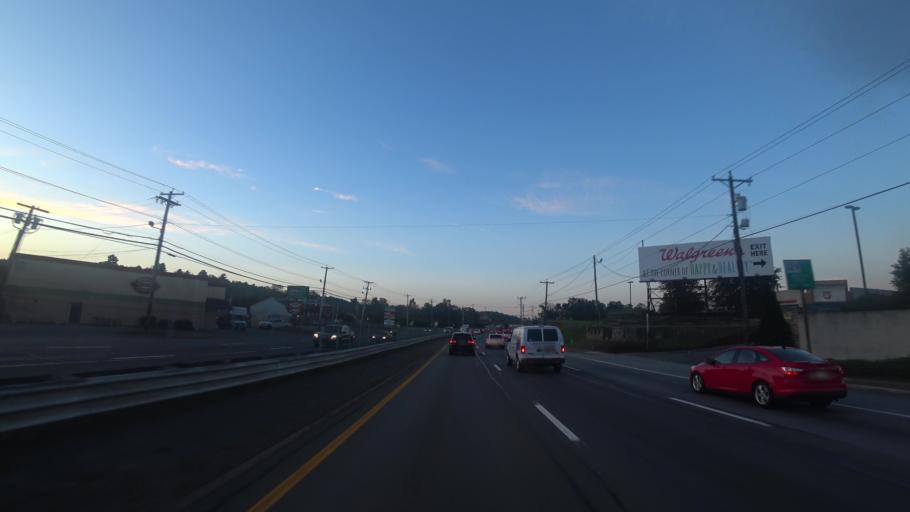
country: US
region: Massachusetts
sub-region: Essex County
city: Saugus
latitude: 42.4916
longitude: -71.0167
